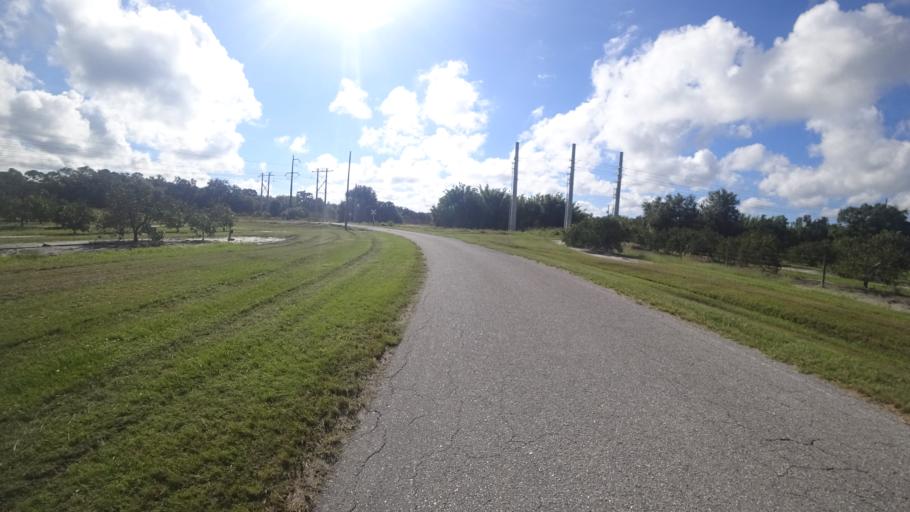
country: US
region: Florida
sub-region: Manatee County
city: Ellenton
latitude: 27.5797
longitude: -82.4604
